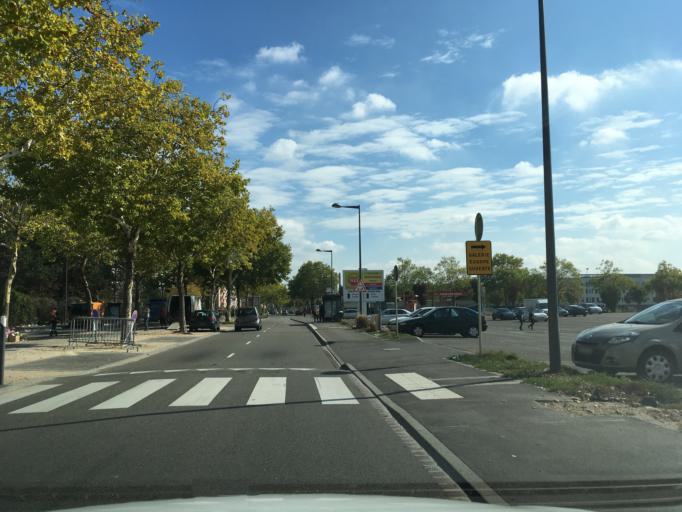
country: FR
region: Alsace
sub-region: Departement du Haut-Rhin
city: Ingersheim
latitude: 48.0787
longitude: 7.3312
